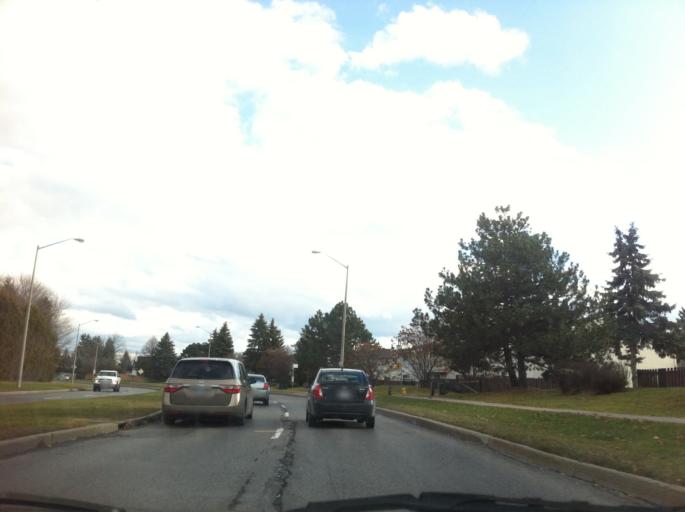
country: CA
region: Quebec
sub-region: Outaouais
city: Gatineau
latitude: 45.4613
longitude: -75.5312
